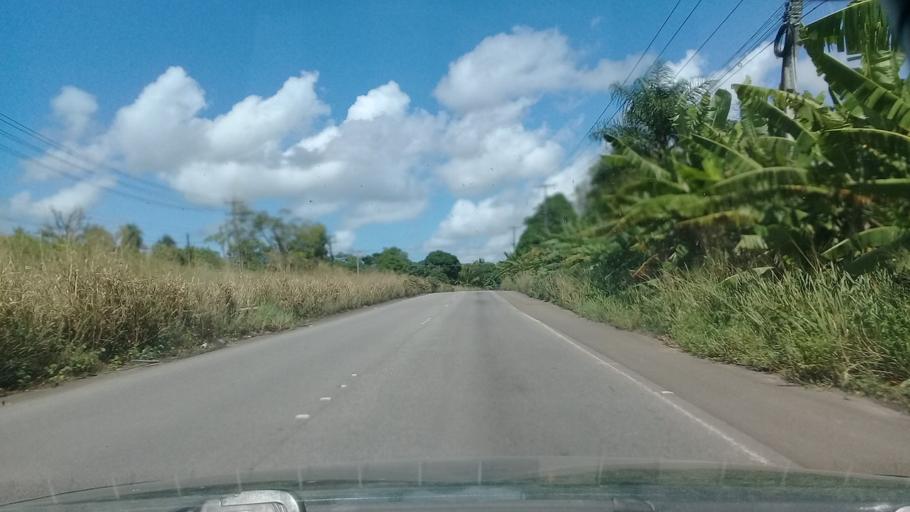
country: BR
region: Pernambuco
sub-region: Cabo De Santo Agostinho
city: Cabo
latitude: -8.3305
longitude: -35.0101
